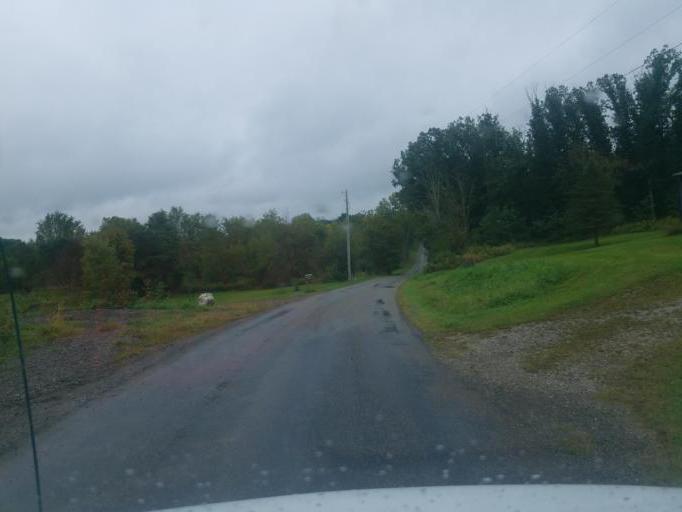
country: US
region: Ohio
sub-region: Wayne County
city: West Salem
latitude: 40.9361
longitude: -82.1226
